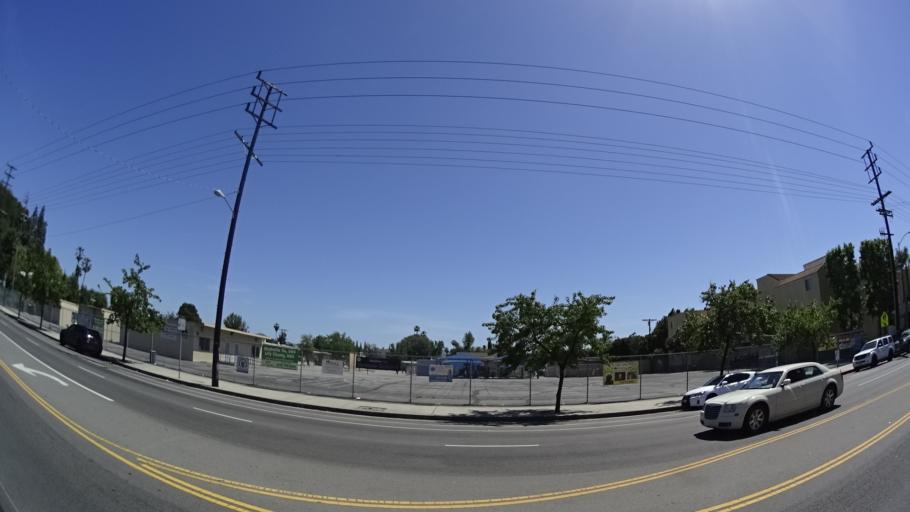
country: US
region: California
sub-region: Los Angeles County
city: North Hollywood
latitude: 34.1722
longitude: -118.3996
